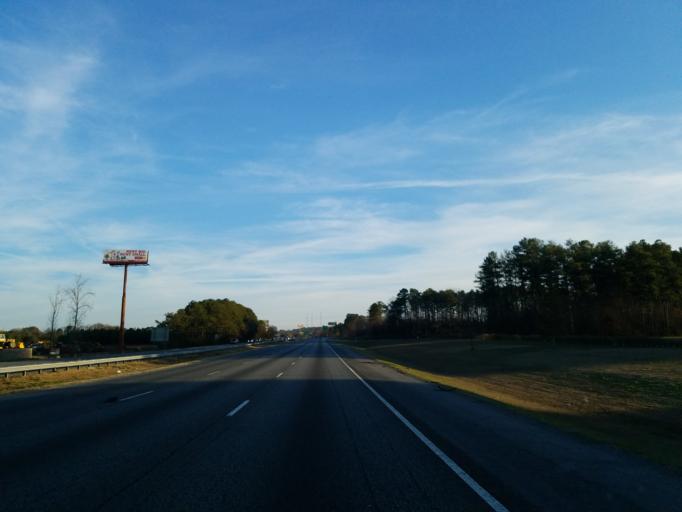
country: US
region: Georgia
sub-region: Gordon County
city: Calhoun
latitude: 34.5657
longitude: -84.9430
